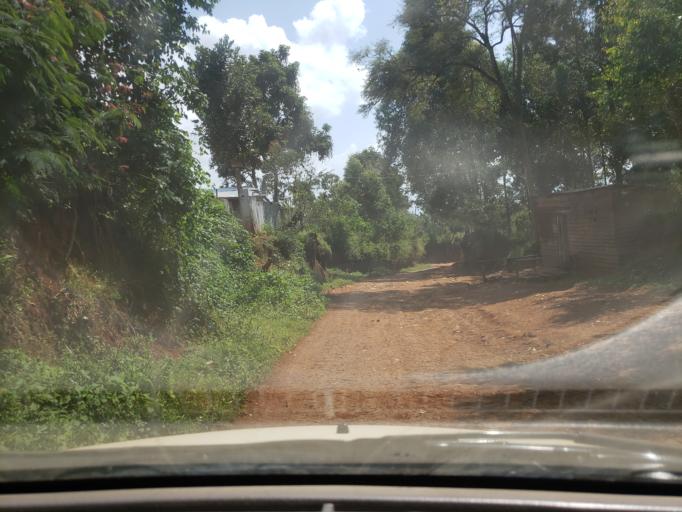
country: CD
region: South Kivu
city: Bukavu
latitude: -2.5037
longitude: 28.8255
